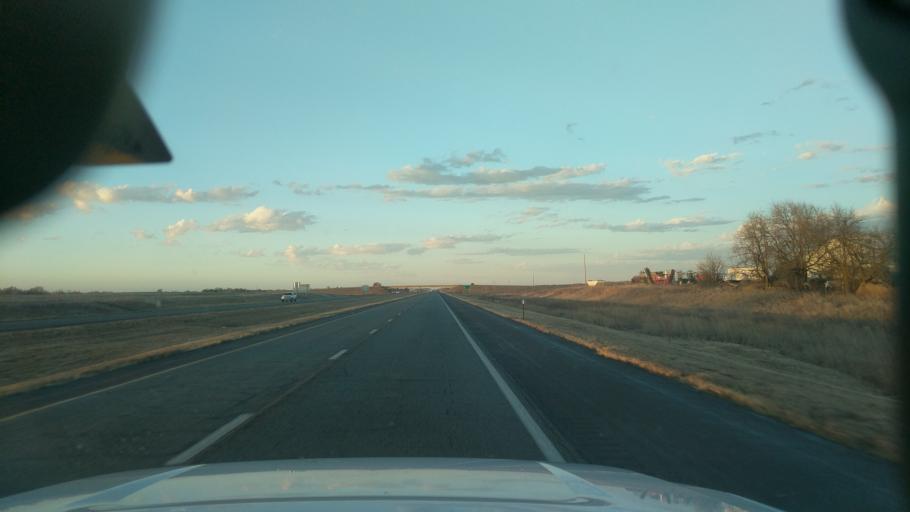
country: US
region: Kansas
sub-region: McPherson County
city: Lindsborg
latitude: 38.5594
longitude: -97.6209
